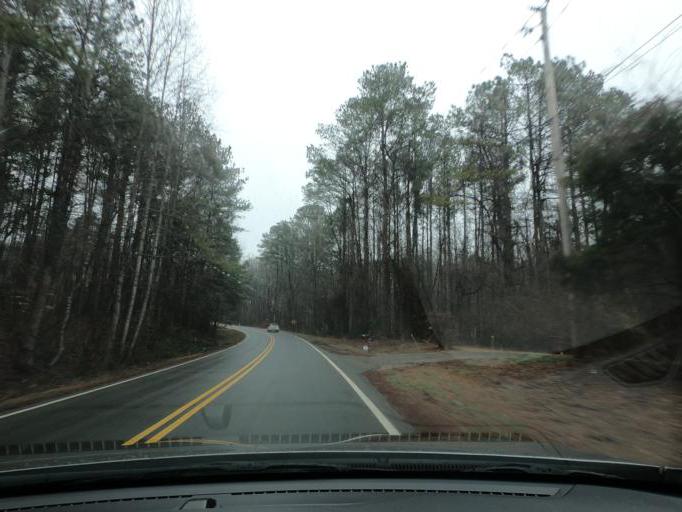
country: US
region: Georgia
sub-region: Fulton County
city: Milton
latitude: 34.1221
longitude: -84.3040
